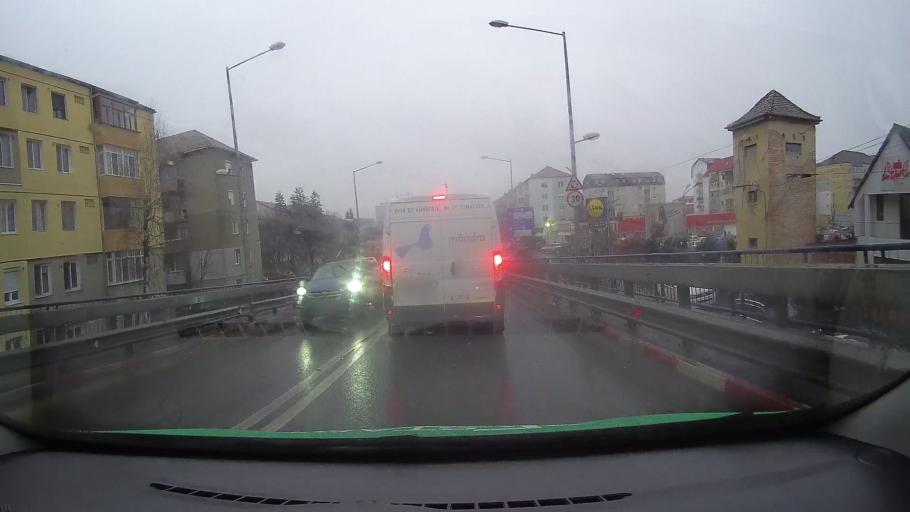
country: RO
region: Sibiu
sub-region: Municipiul Sibiu
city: Sibiu
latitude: 45.8100
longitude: 24.1474
